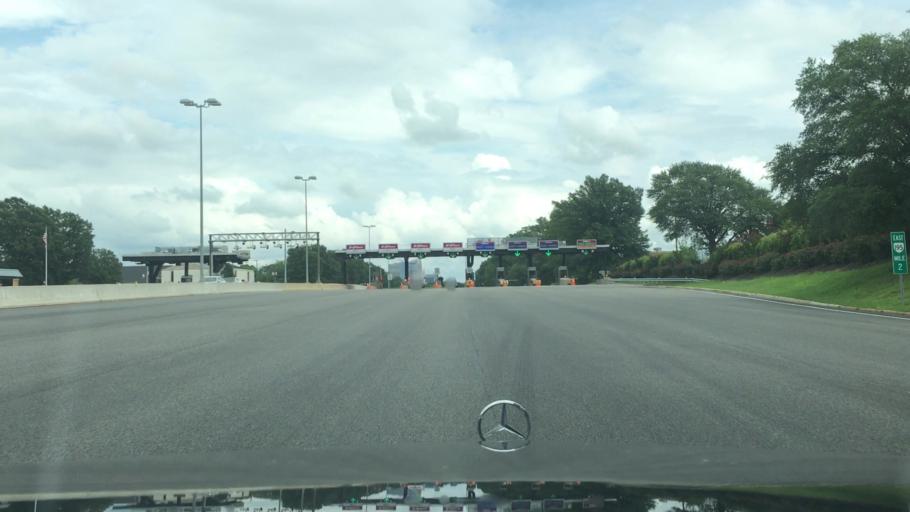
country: US
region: Virginia
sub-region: City of Richmond
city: Richmond
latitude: 37.5454
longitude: -77.4633
